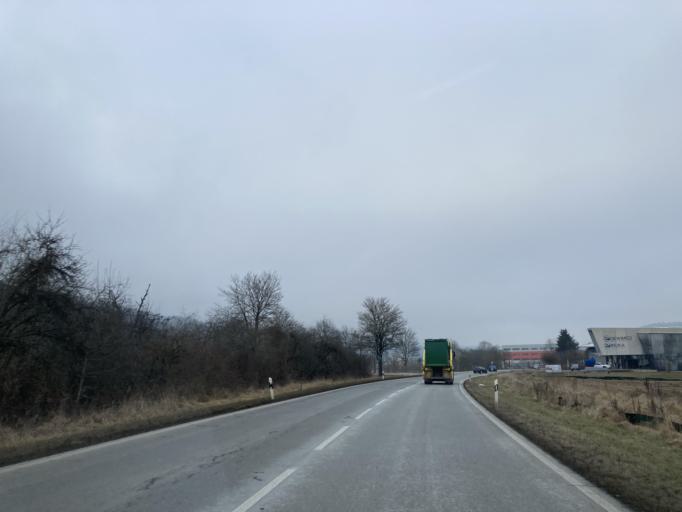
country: DE
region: Baden-Wuerttemberg
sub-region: Freiburg Region
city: Wurmlingen
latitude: 47.9568
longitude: 8.7763
